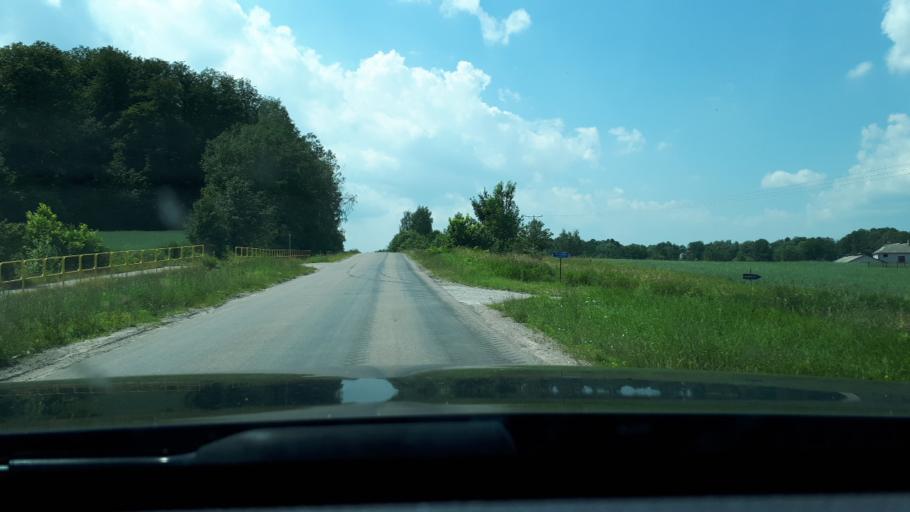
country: PL
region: Podlasie
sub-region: Powiat bialostocki
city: Choroszcz
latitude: 53.1246
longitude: 22.9552
